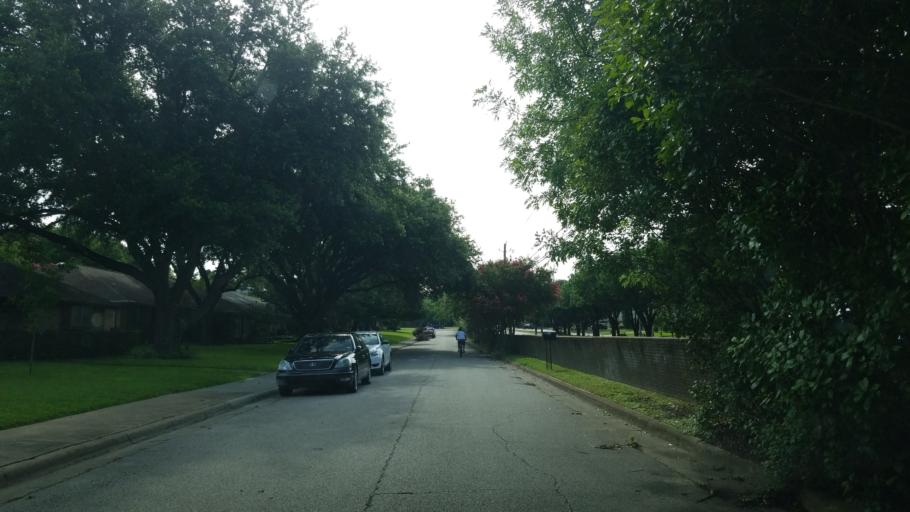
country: US
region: Texas
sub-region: Dallas County
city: Farmers Branch
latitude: 32.8952
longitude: -96.8494
